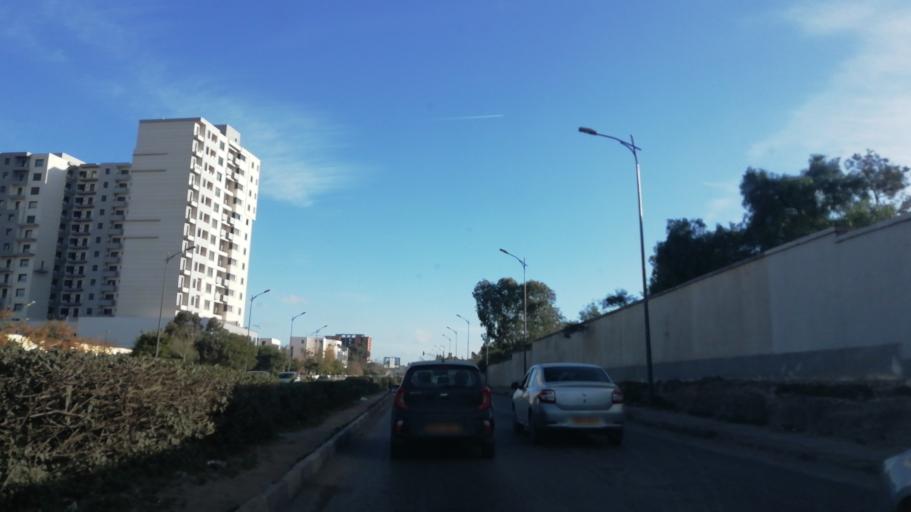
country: DZ
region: Oran
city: Bir el Djir
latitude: 35.7132
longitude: -0.5768
